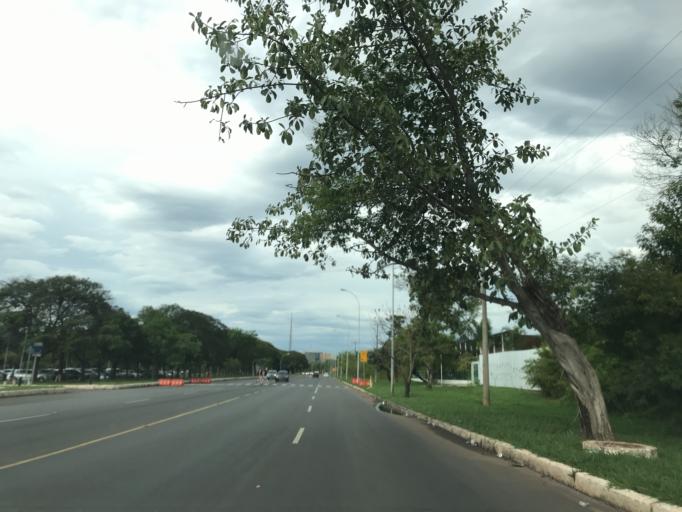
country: BR
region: Federal District
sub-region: Brasilia
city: Brasilia
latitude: -15.8042
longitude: -47.9059
